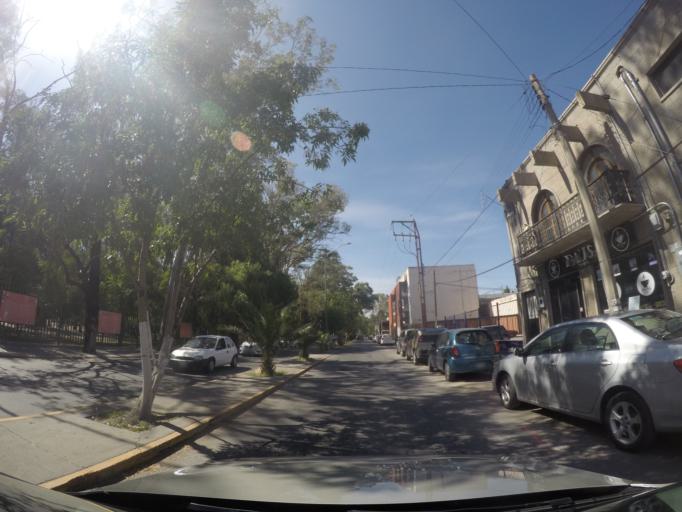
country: MX
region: San Luis Potosi
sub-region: San Luis Potosi
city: San Luis Potosi
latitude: 22.1490
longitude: -101.0149
